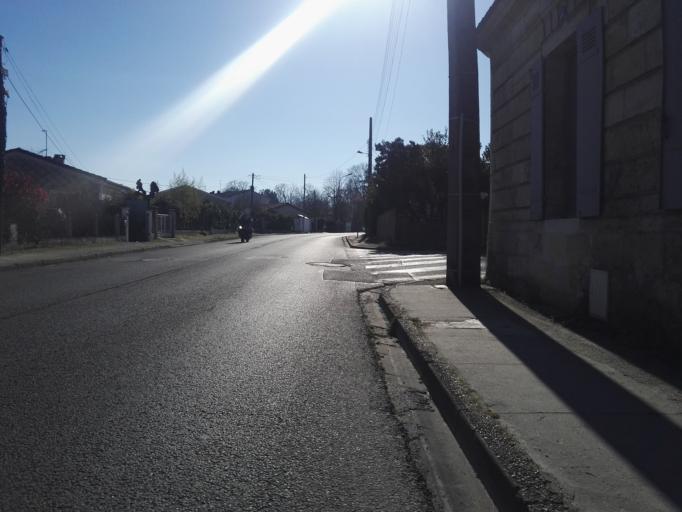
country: FR
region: Aquitaine
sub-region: Departement de la Gironde
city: Talence
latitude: 44.8029
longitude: -0.5862
